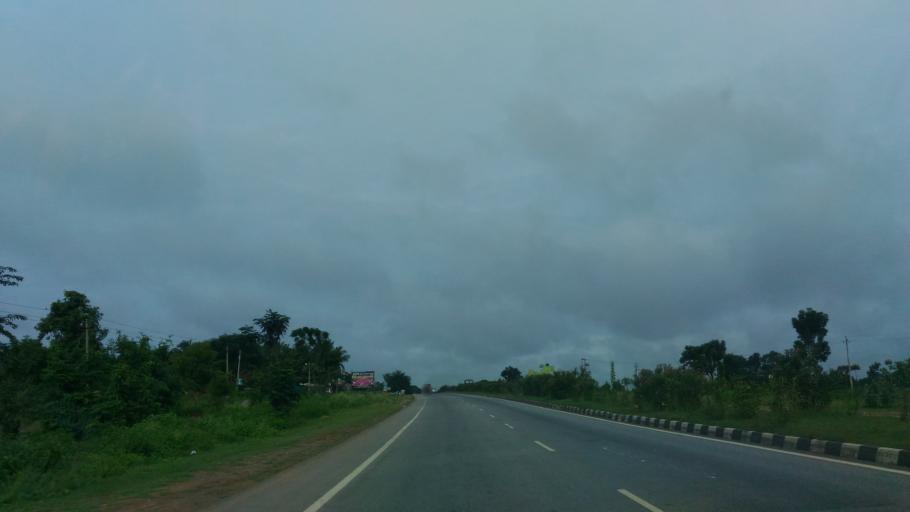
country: IN
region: Karnataka
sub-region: Tumkur
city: Kunigal
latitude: 13.0375
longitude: 77.0998
